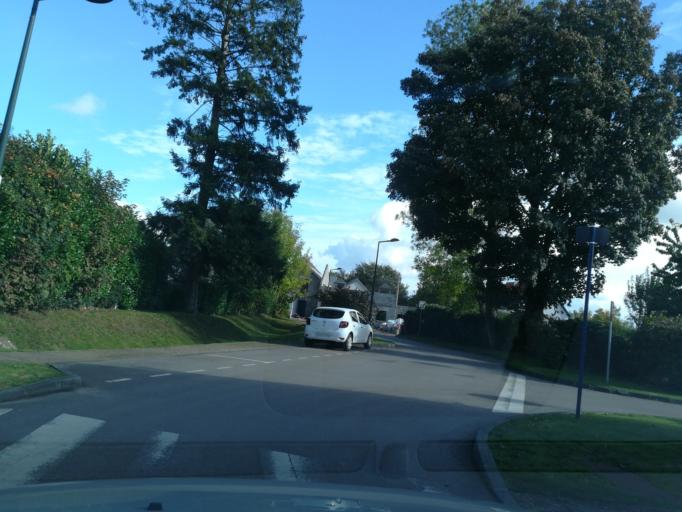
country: FR
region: Haute-Normandie
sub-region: Departement de la Seine-Maritime
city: Bois-Guillaume
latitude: 49.4730
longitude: 1.1314
